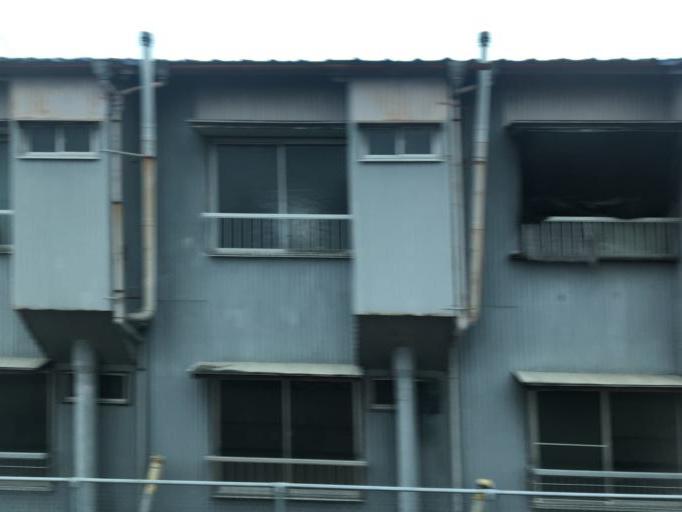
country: JP
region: Tochigi
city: Oyama
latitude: 36.3082
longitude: 139.8064
